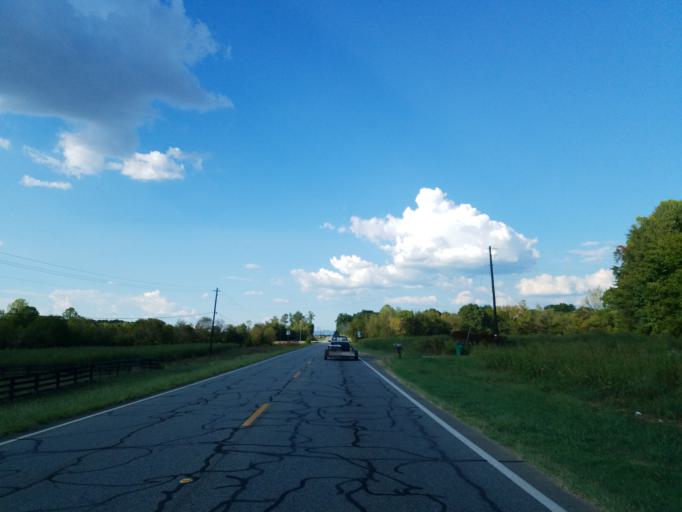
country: US
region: Georgia
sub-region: Bartow County
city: Rydal
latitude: 34.5261
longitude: -84.7066
